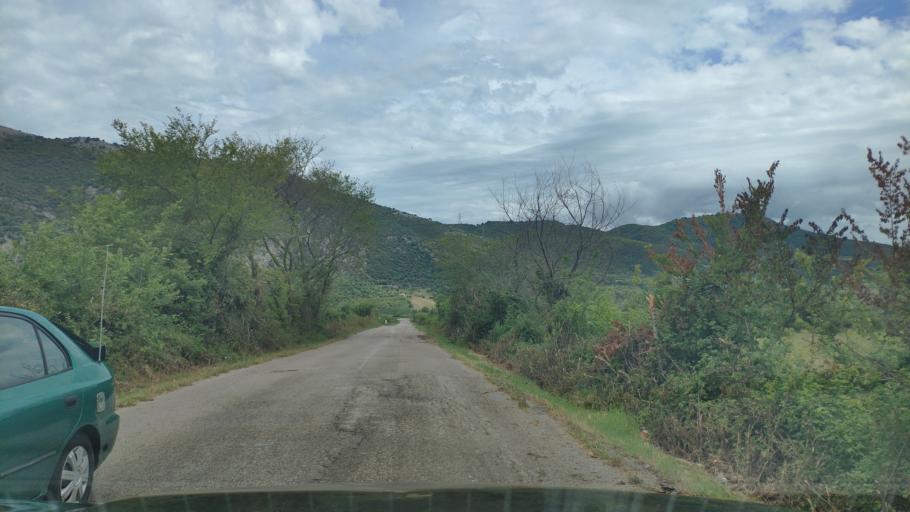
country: GR
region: West Greece
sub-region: Nomos Aitolias kai Akarnanias
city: Vonitsa
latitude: 38.9102
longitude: 20.9020
